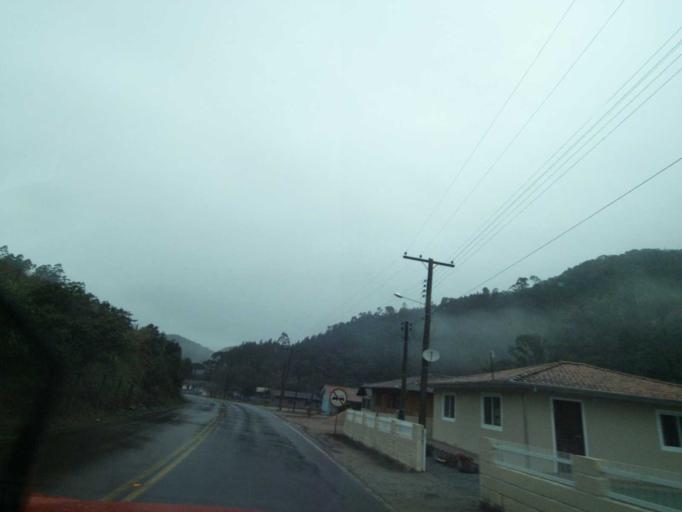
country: BR
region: Santa Catarina
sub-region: Anitapolis
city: Anitapolis
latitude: -27.8347
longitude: -49.0525
